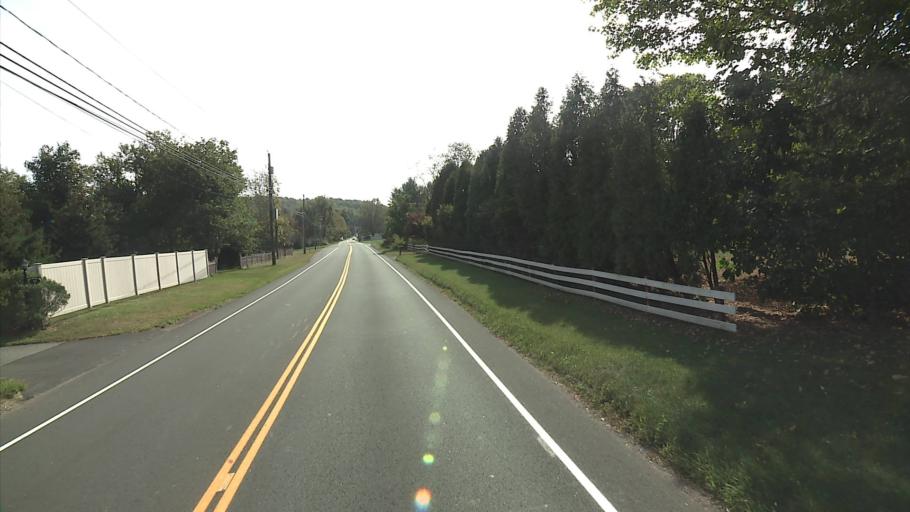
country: US
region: Connecticut
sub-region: Fairfield County
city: Newtown
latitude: 41.4060
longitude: -73.2543
